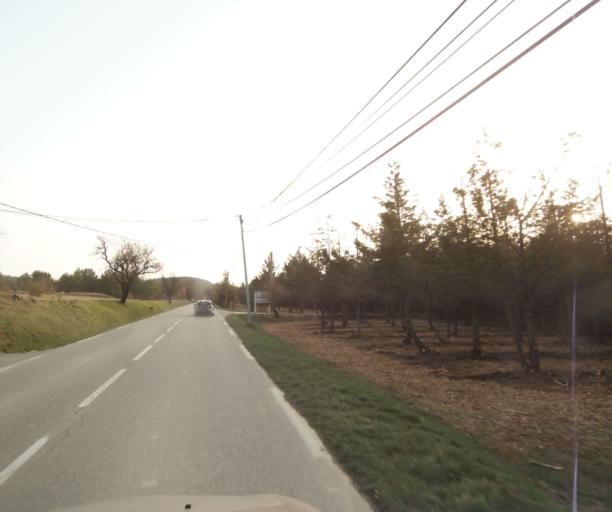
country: FR
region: Provence-Alpes-Cote d'Azur
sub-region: Departement des Bouches-du-Rhone
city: Rognes
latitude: 43.6925
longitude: 5.3433
